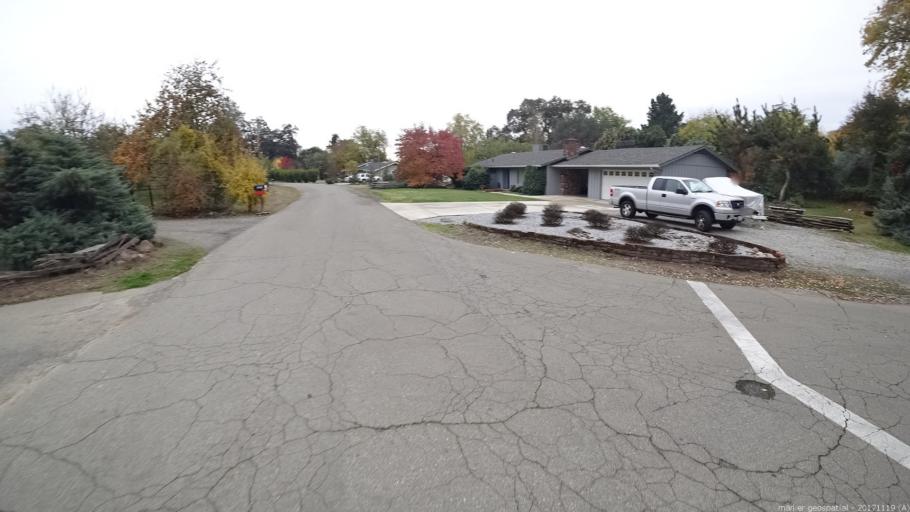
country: US
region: California
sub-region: Shasta County
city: Anderson
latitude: 40.4936
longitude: -122.3479
